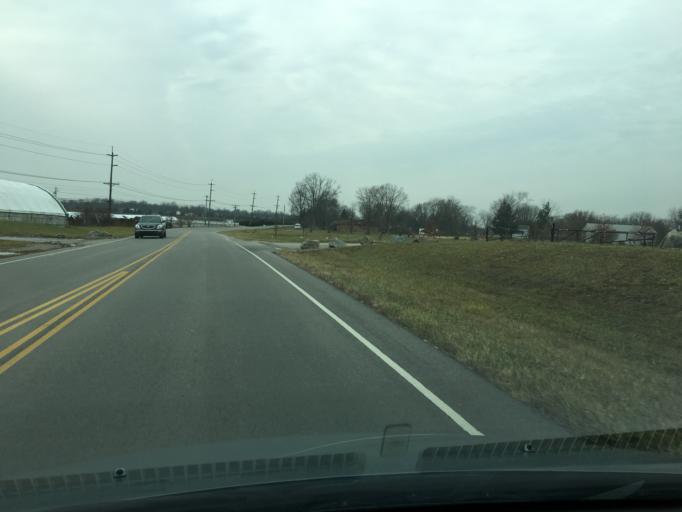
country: US
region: Ohio
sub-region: Hamilton County
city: Highpoint
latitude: 39.3193
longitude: -84.3335
